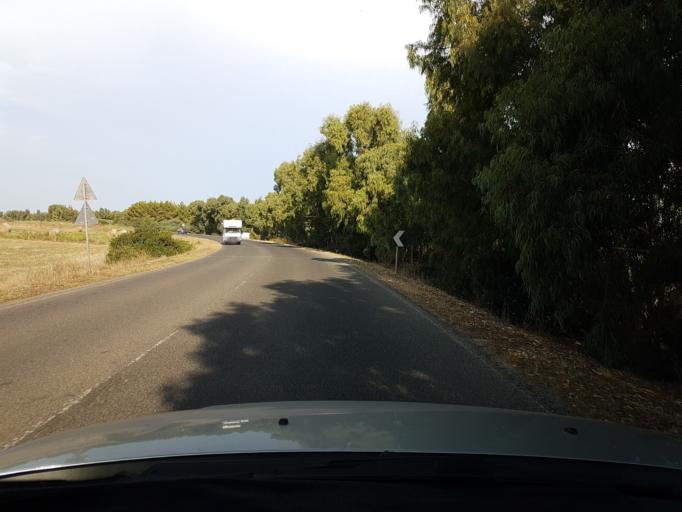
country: IT
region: Sardinia
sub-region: Provincia di Oristano
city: Cabras
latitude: 39.9185
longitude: 8.4959
